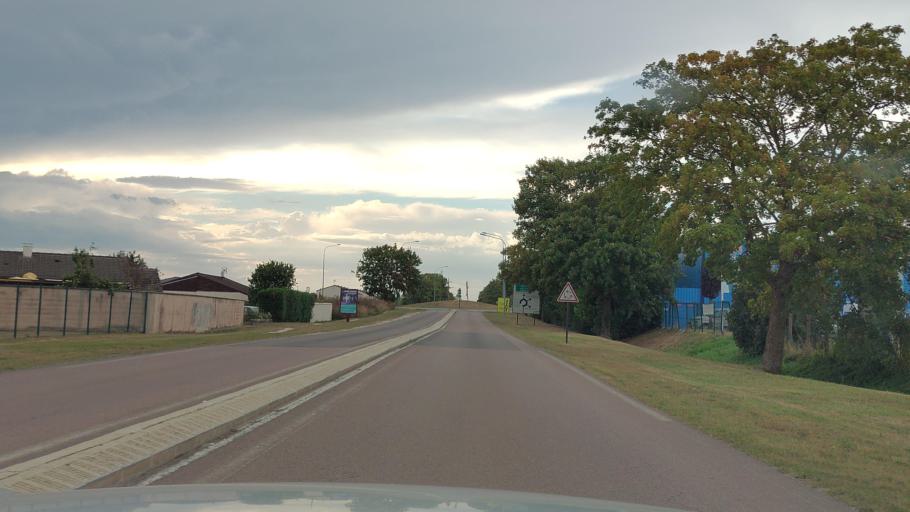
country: FR
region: Ile-de-France
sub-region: Departement de Seine-et-Marne
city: Mormant
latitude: 48.6129
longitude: 2.8819
